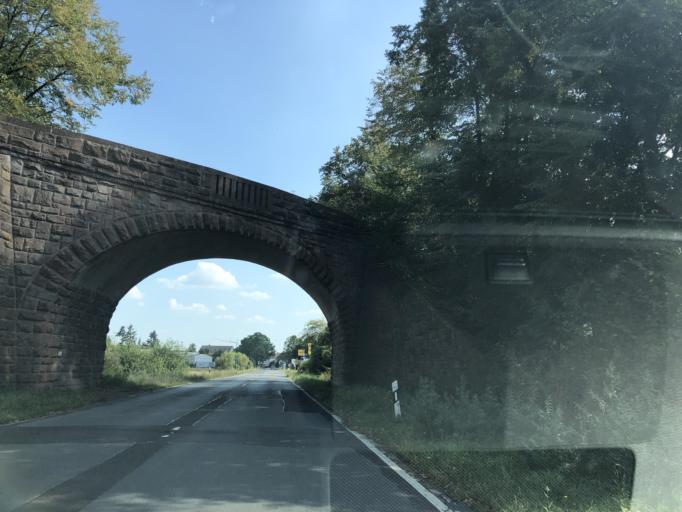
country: DE
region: Hesse
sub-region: Regierungsbezirk Giessen
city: Kirchhain
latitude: 50.8298
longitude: 8.9077
